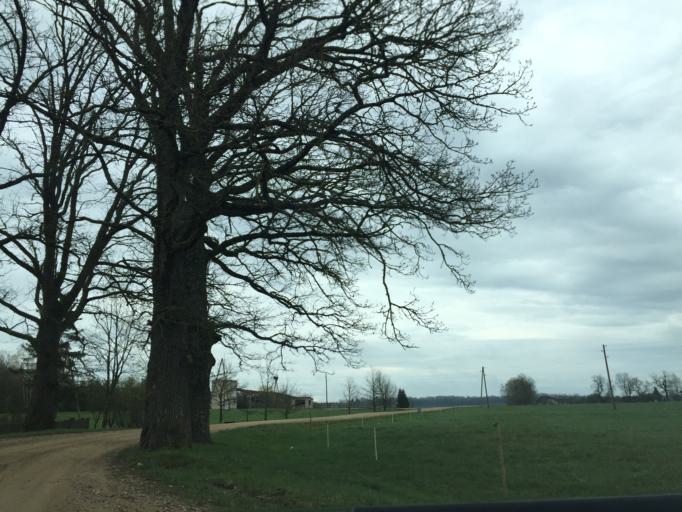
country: LV
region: Sigulda
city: Sigulda
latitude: 57.0442
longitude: 24.8384
